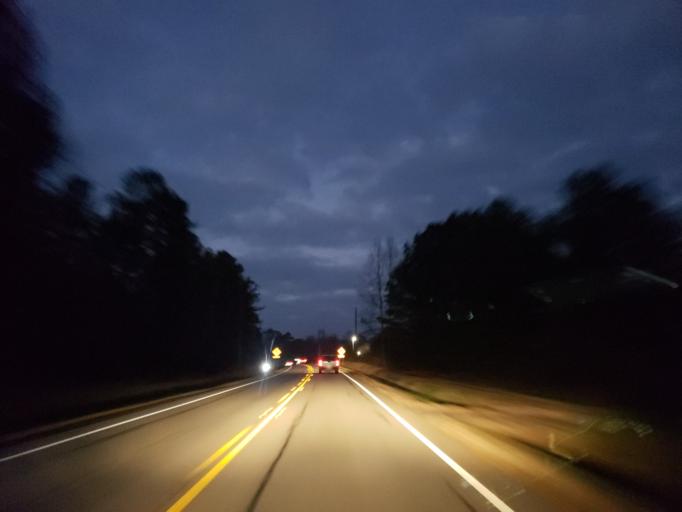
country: US
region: Georgia
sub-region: Polk County
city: Rockmart
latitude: 33.9131
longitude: -84.9922
